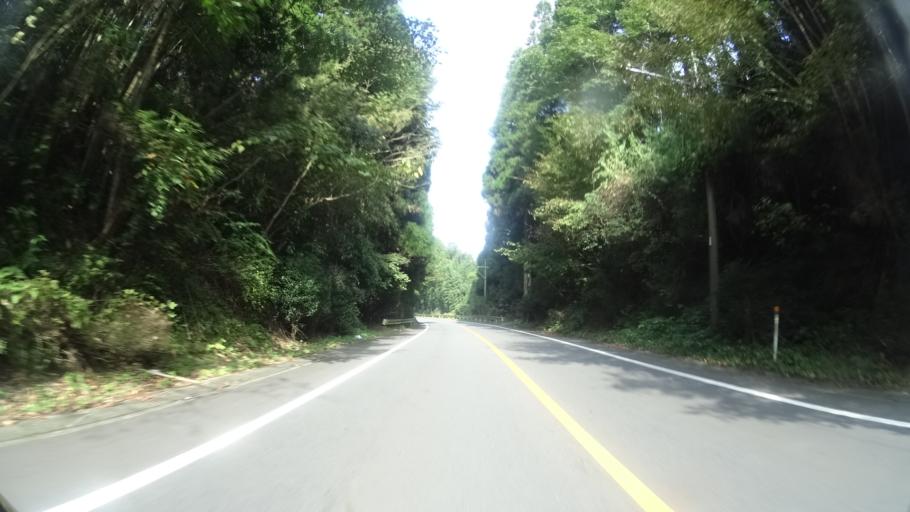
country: JP
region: Kumamoto
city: Aso
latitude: 33.0833
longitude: 131.0645
